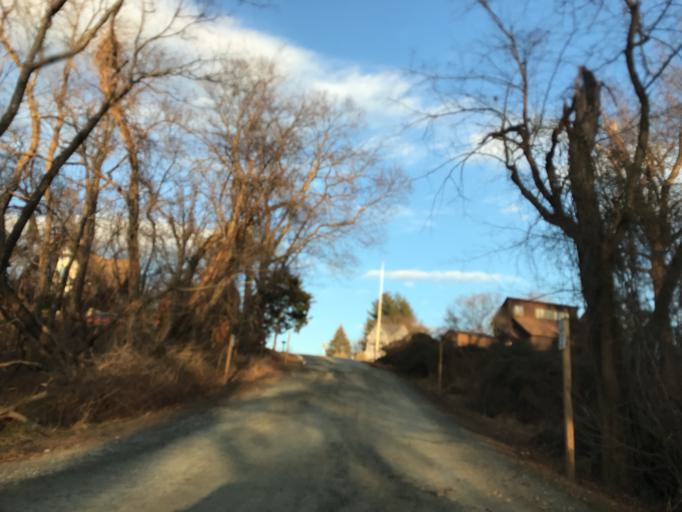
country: US
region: Maryland
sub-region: Cecil County
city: Charlestown
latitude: 39.4601
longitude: -76.0054
